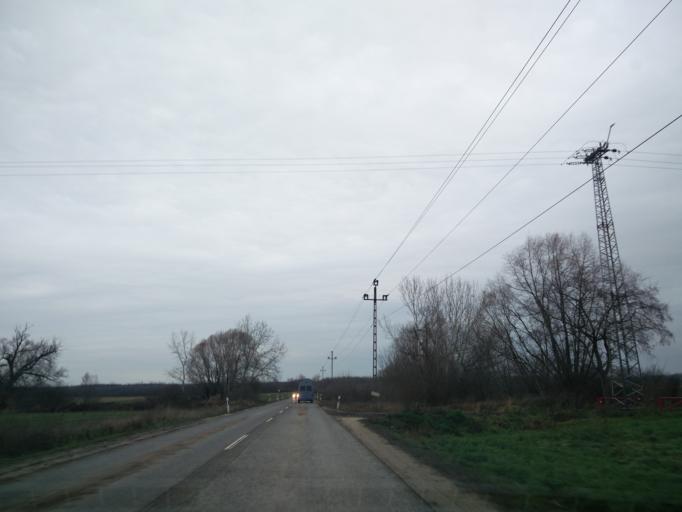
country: HU
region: Pest
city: Ullo
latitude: 47.3983
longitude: 19.3710
